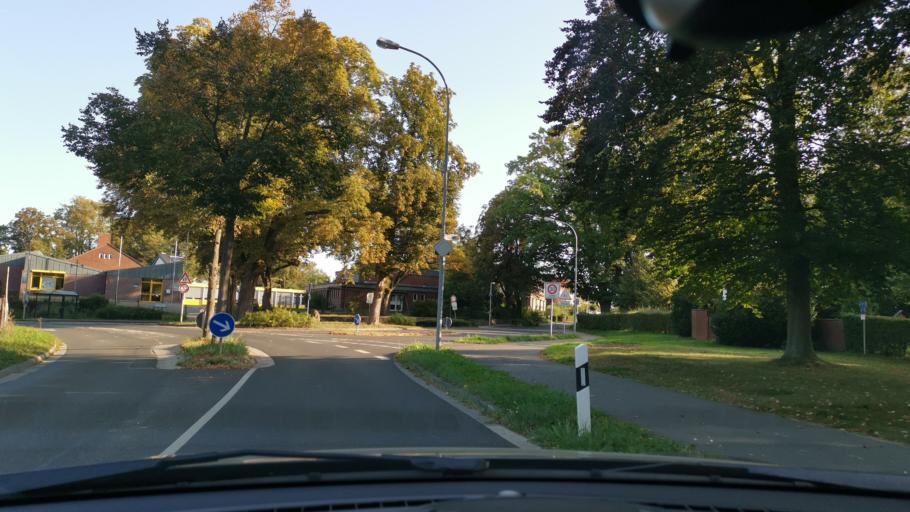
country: DE
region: North Rhine-Westphalia
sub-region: Regierungsbezirk Dusseldorf
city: Rommerskirchen
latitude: 51.0910
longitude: 6.6908
